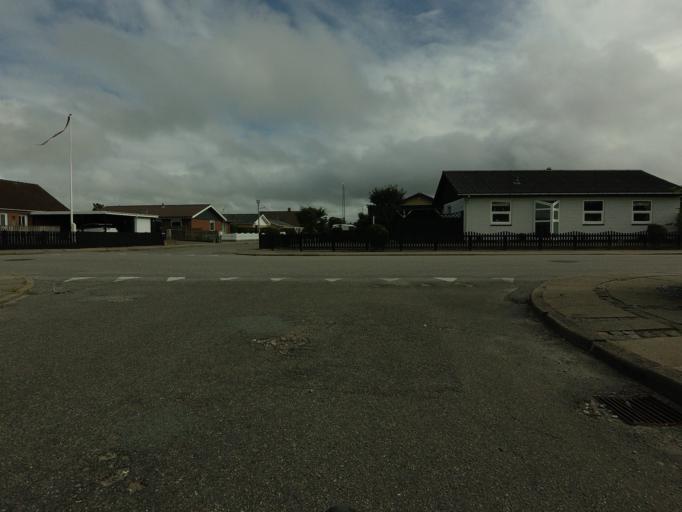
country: DK
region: North Denmark
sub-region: Jammerbugt Kommune
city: Pandrup
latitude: 57.3699
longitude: 9.7211
